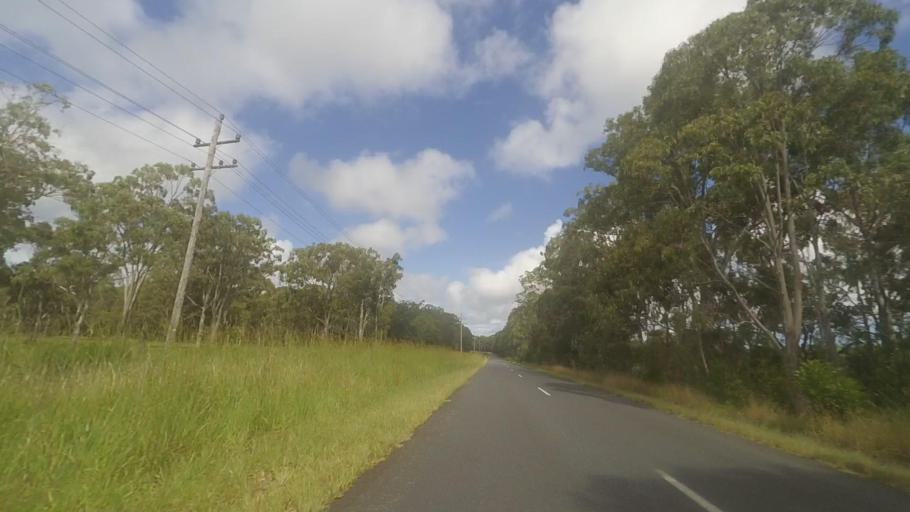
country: AU
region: New South Wales
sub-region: Great Lakes
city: Bulahdelah
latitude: -32.3822
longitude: 152.3927
